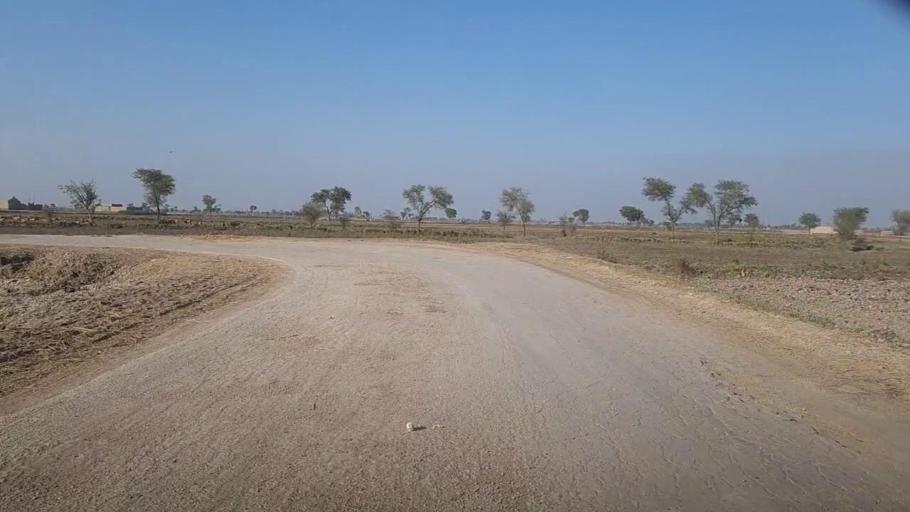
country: PK
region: Sindh
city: Phulji
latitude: 26.8660
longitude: 67.7947
